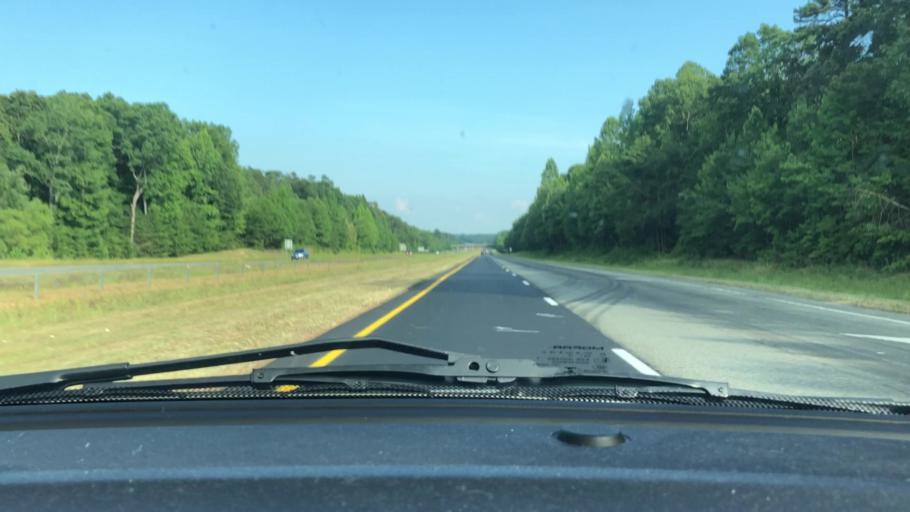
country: US
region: North Carolina
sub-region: Randolph County
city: Liberty
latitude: 35.8100
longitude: -79.5481
